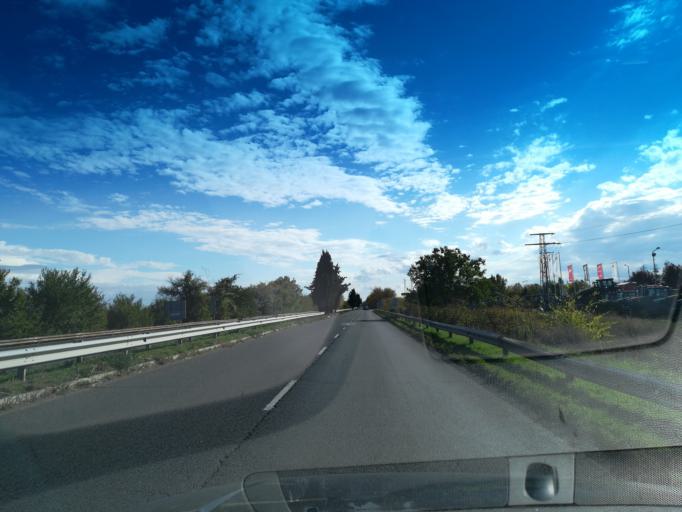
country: BG
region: Stara Zagora
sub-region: Obshtina Stara Zagora
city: Stara Zagora
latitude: 42.3907
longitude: 25.6470
